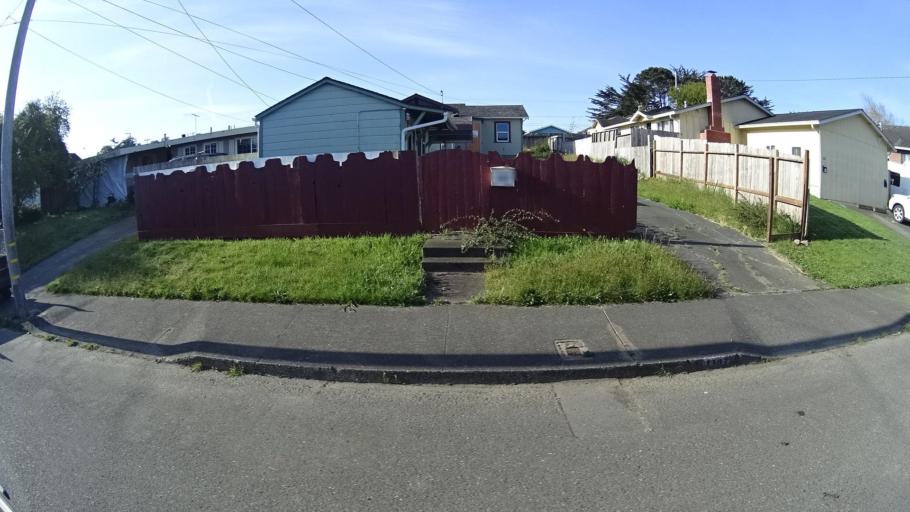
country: US
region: California
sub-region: Humboldt County
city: Bayview
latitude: 40.7741
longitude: -124.1855
